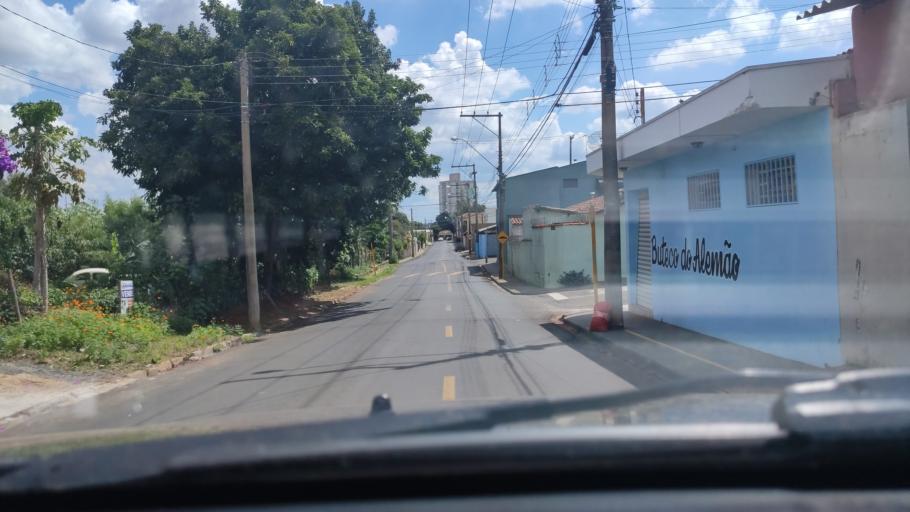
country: BR
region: Sao Paulo
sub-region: Sao Carlos
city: Sao Carlos
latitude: -22.0068
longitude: -47.8773
